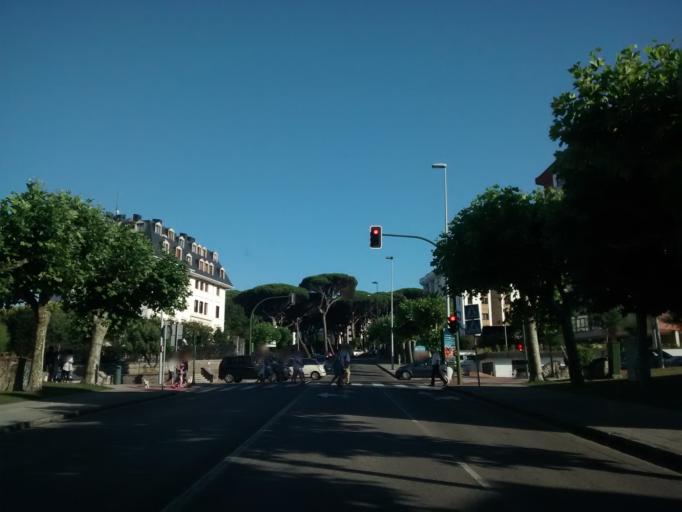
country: ES
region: Cantabria
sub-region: Provincia de Cantabria
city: Santander
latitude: 43.4736
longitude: -3.7886
